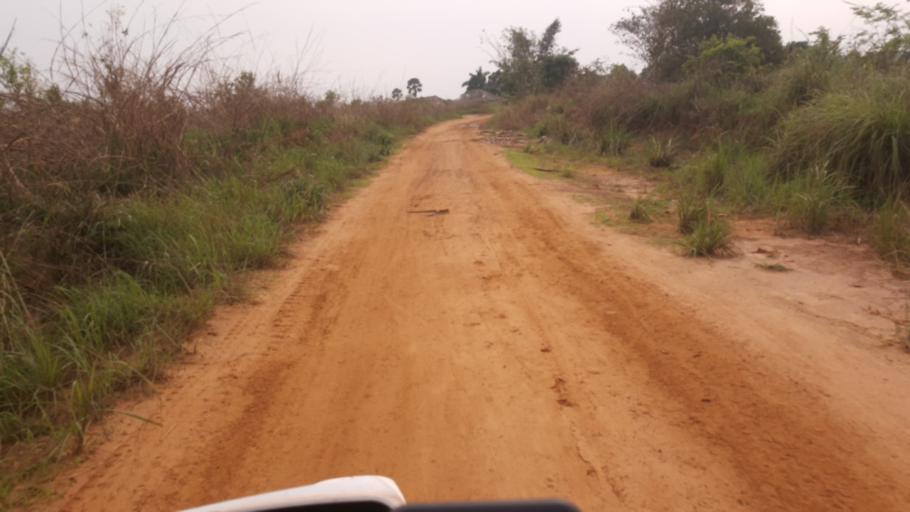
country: CD
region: Bandundu
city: Bandundu
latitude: -3.4602
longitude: 17.7208
